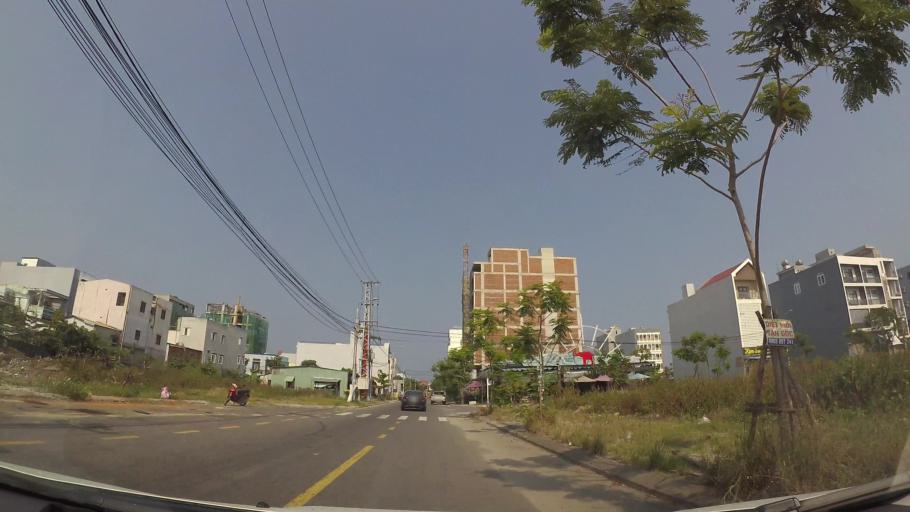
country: VN
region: Da Nang
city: Ngu Hanh Son
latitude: 16.0379
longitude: 108.2460
